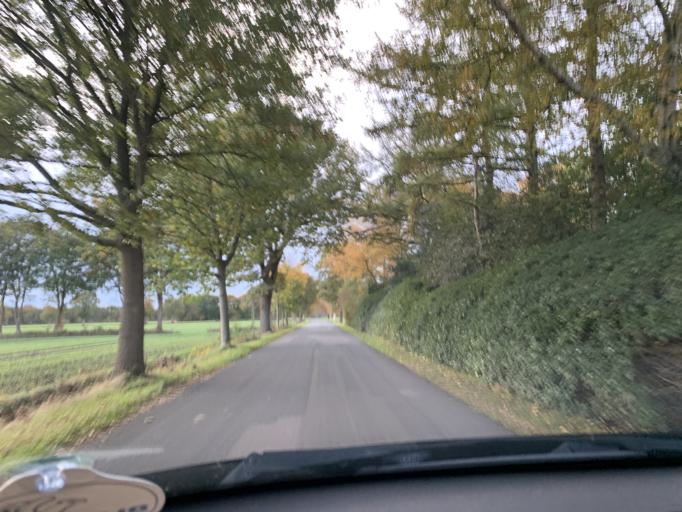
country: DE
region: Lower Saxony
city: Wiefelstede
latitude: 53.2640
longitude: 8.0927
